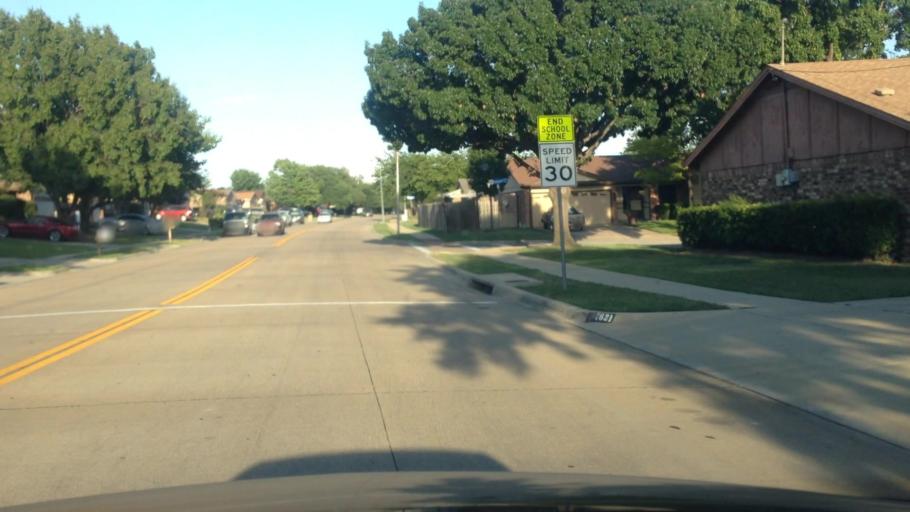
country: US
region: Texas
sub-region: Tarrant County
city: Watauga
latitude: 32.8822
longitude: -97.2484
